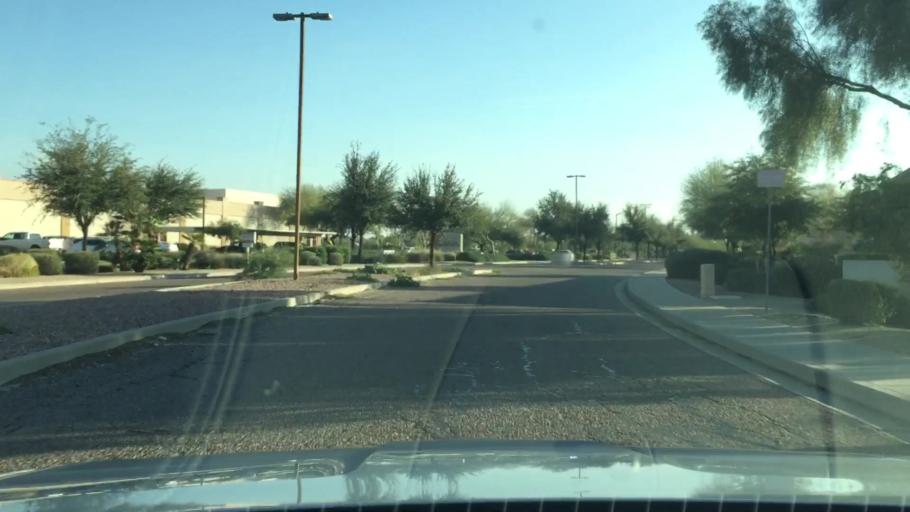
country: US
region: Arizona
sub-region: Maricopa County
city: Gilbert
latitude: 33.3811
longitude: -111.7356
